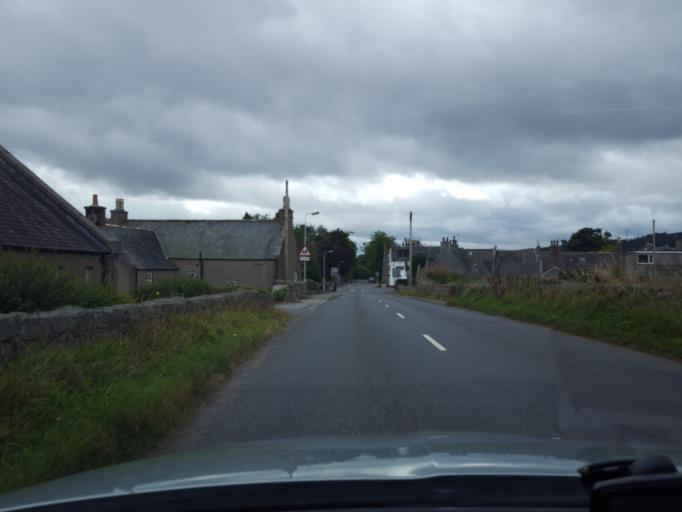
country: GB
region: Scotland
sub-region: Aberdeenshire
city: Kemnay
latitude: 57.1426
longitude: -2.4339
